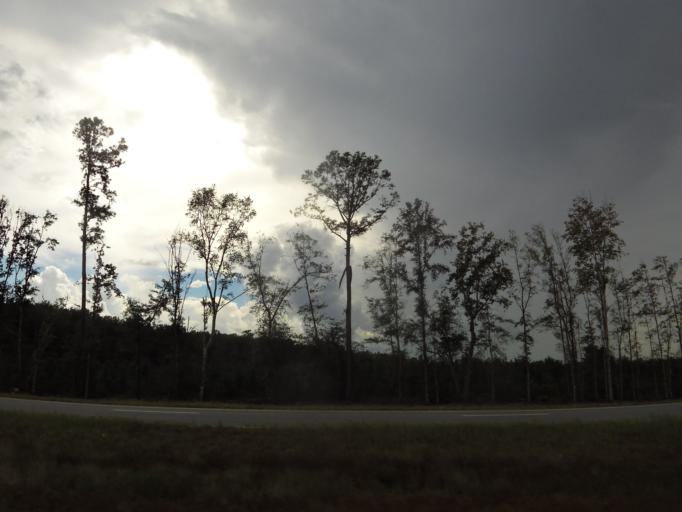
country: US
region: Georgia
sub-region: Glynn County
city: Dock Junction
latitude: 31.3488
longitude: -81.6081
